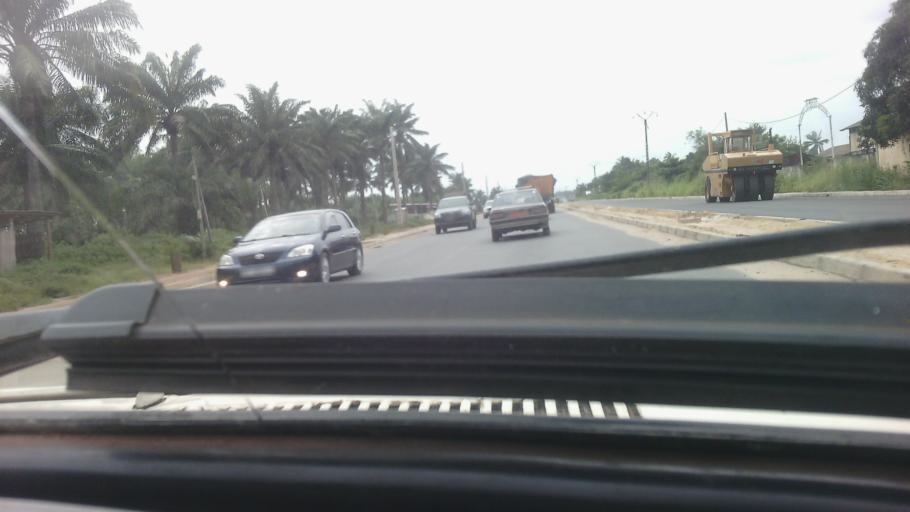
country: BJ
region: Atlantique
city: Hevie
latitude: 6.3821
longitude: 2.1743
